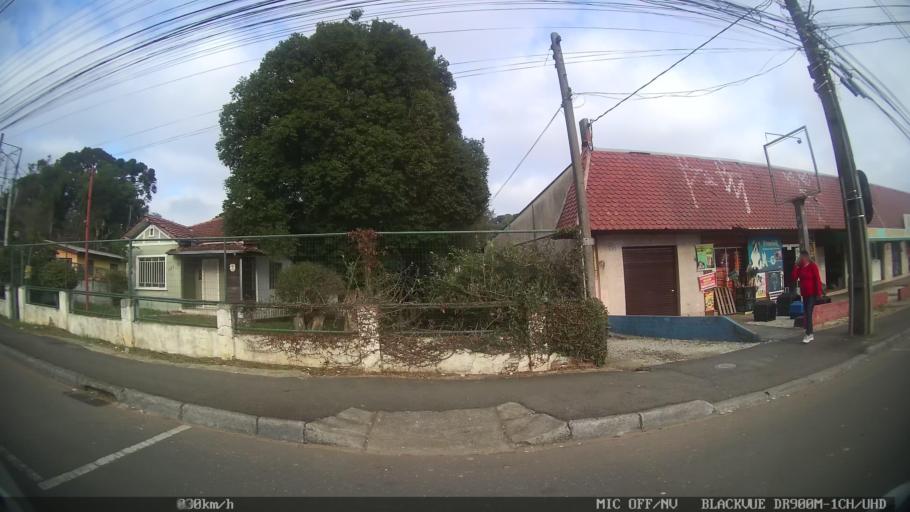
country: BR
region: Parana
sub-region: Curitiba
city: Curitiba
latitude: -25.3990
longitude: -49.3145
